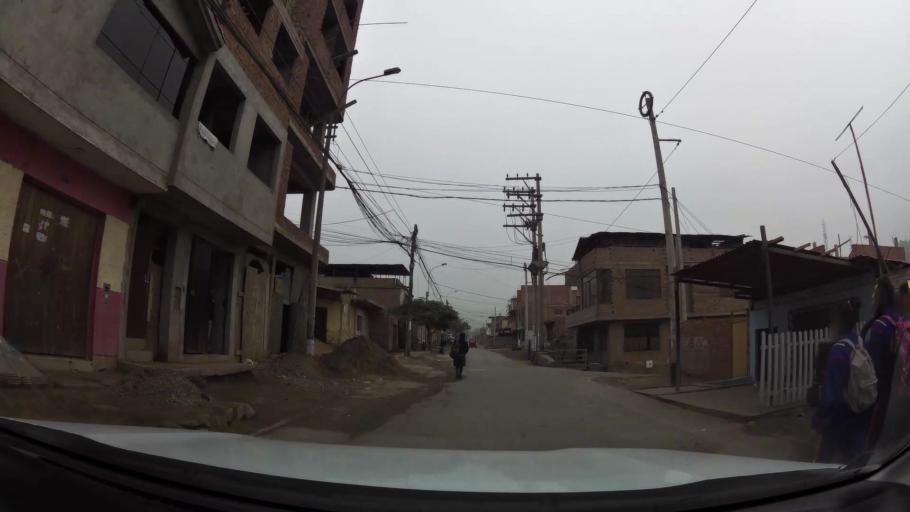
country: PE
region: Lima
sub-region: Lima
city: Surco
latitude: -12.1761
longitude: -76.9385
